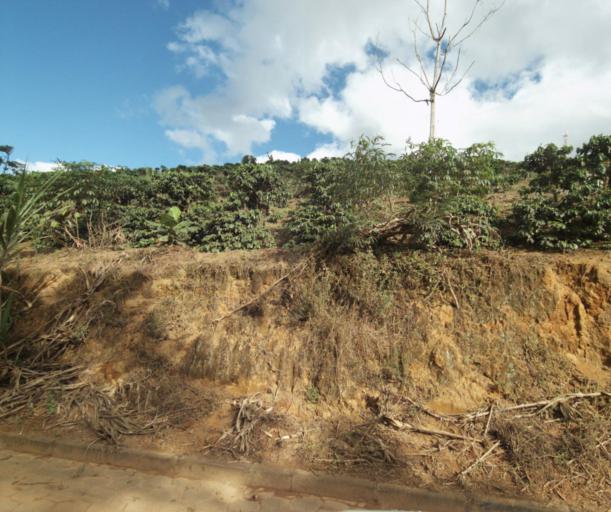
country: BR
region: Espirito Santo
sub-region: Irupi
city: Irupi
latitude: -20.5416
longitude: -41.6701
